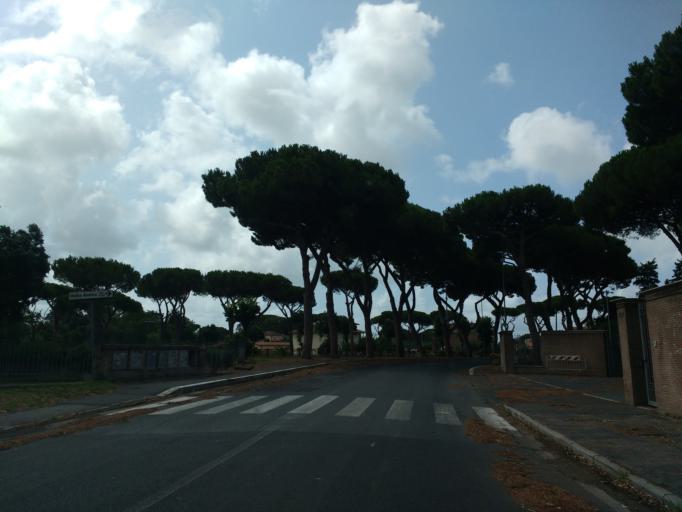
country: IT
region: Latium
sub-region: Citta metropolitana di Roma Capitale
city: Acilia-Castel Fusano-Ostia Antica
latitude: 41.7594
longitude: 12.3007
